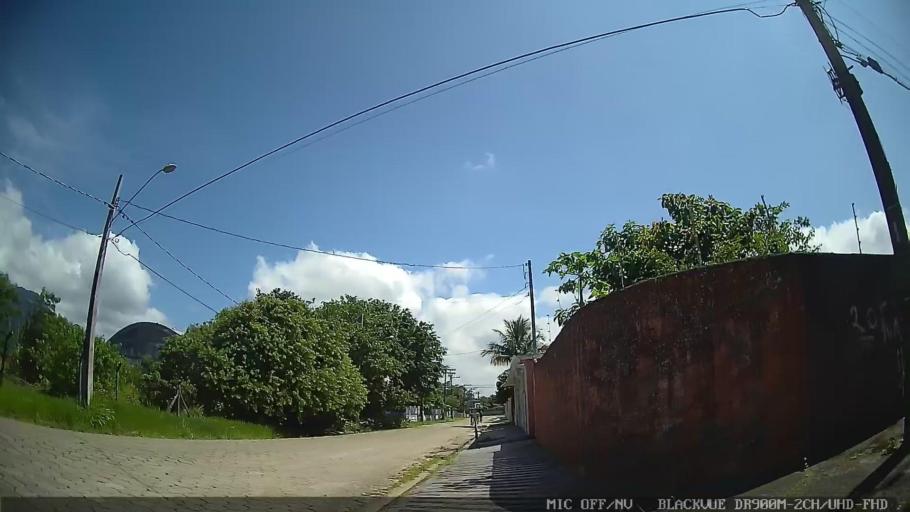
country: BR
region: Sao Paulo
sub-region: Peruibe
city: Peruibe
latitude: -24.3250
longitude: -47.0064
